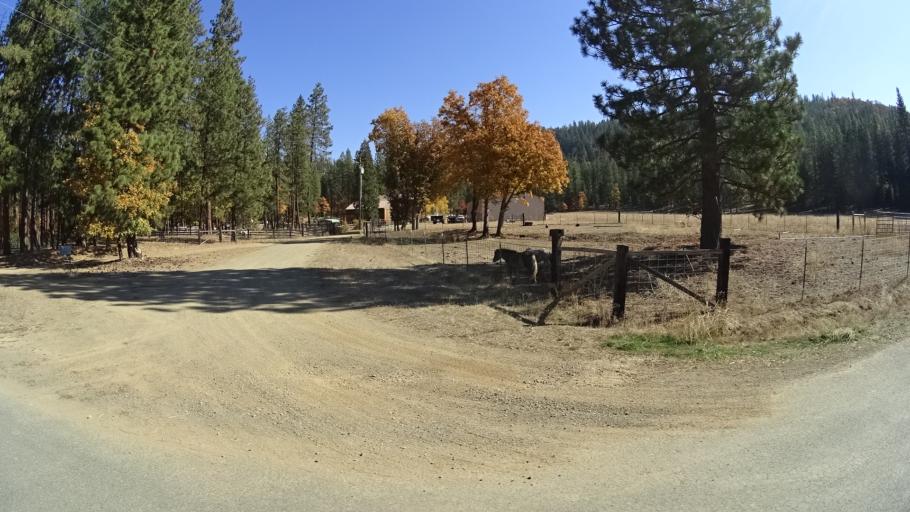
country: US
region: California
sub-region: Siskiyou County
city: Yreka
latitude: 41.6014
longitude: -122.9569
